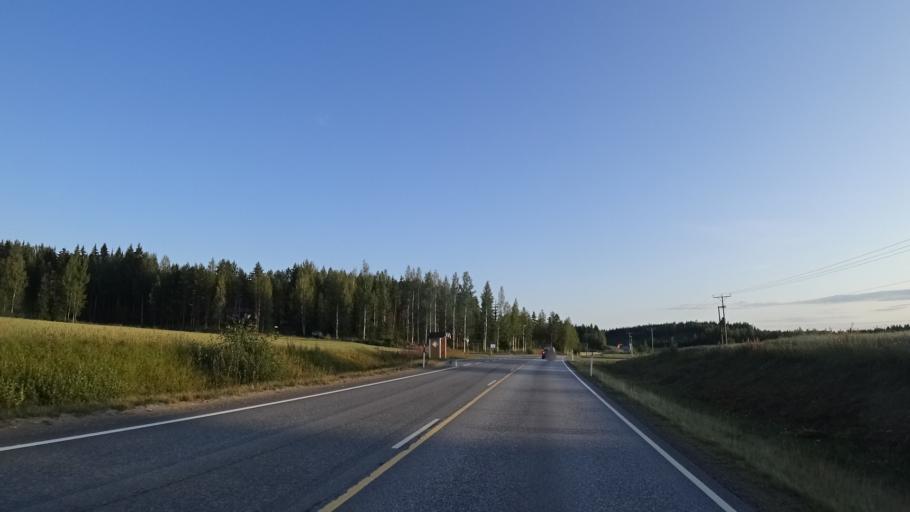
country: FI
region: South Karelia
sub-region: Lappeenranta
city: Ylaemaa
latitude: 60.8592
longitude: 28.1322
